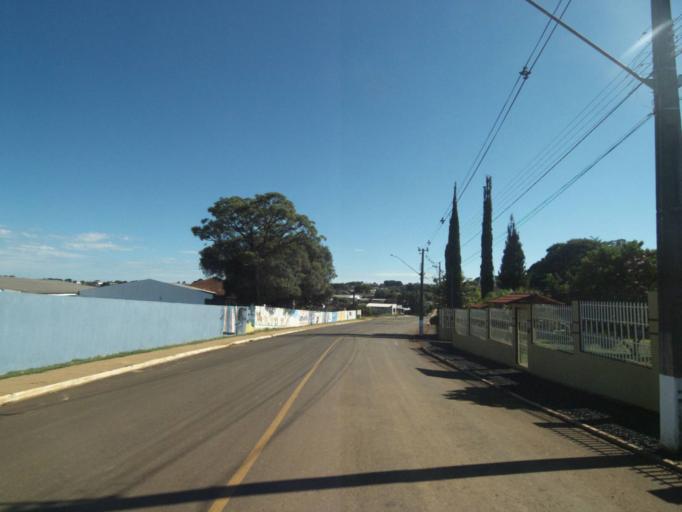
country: BR
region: Parana
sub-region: Pinhao
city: Pinhao
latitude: -25.8422
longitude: -52.0301
